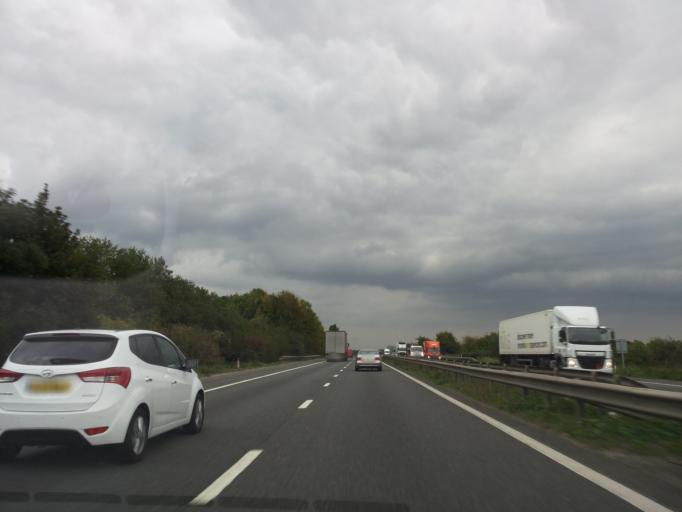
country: GB
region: England
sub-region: Kent
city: Newington
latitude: 51.3252
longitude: 0.6751
